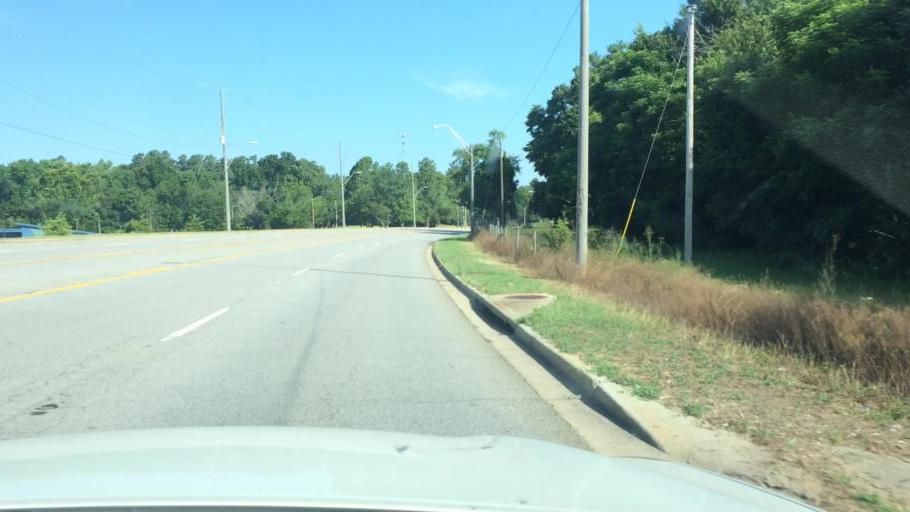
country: US
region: South Carolina
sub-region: Aiken County
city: North Augusta
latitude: 33.5313
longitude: -81.9846
